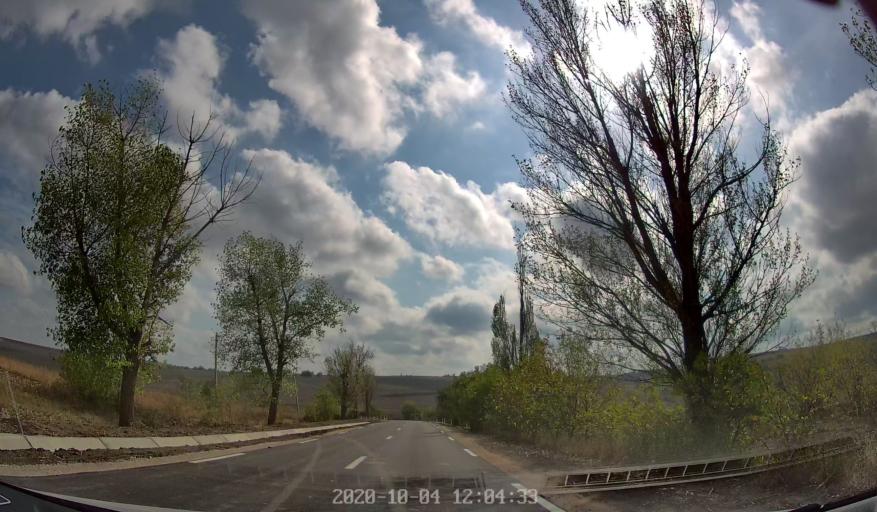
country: MD
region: Rezina
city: Saharna
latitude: 47.6028
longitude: 28.9443
